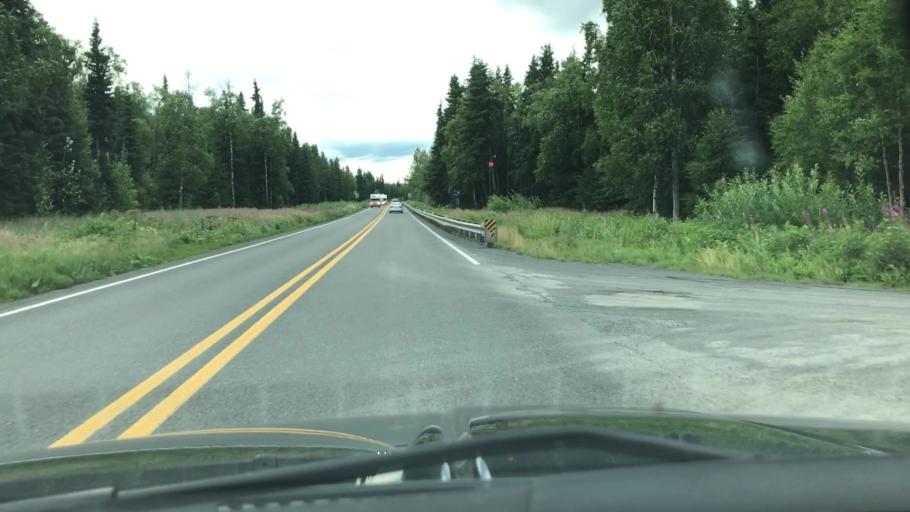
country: US
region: Alaska
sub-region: Kenai Peninsula Borough
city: Seward
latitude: 60.4836
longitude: -149.8912
